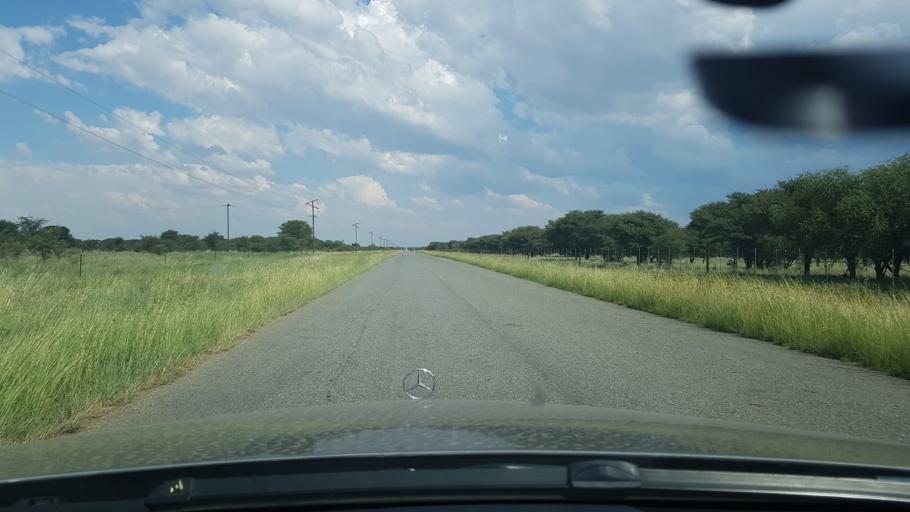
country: ZA
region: North-West
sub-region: Dr Ruth Segomotsi Mompati District Municipality
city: Bloemhof
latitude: -27.7607
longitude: 25.5980
